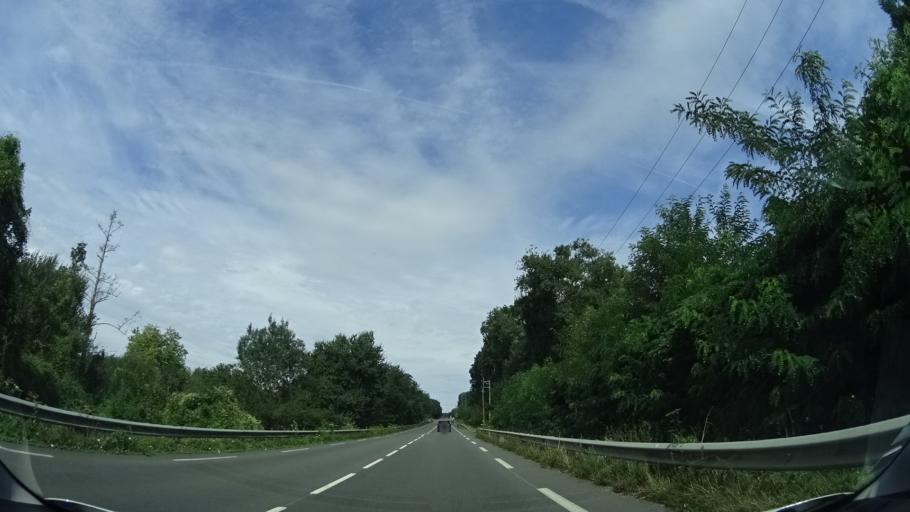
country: FR
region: Pays de la Loire
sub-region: Departement de la Sarthe
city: La Fleche
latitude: 47.7236
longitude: -0.1099
